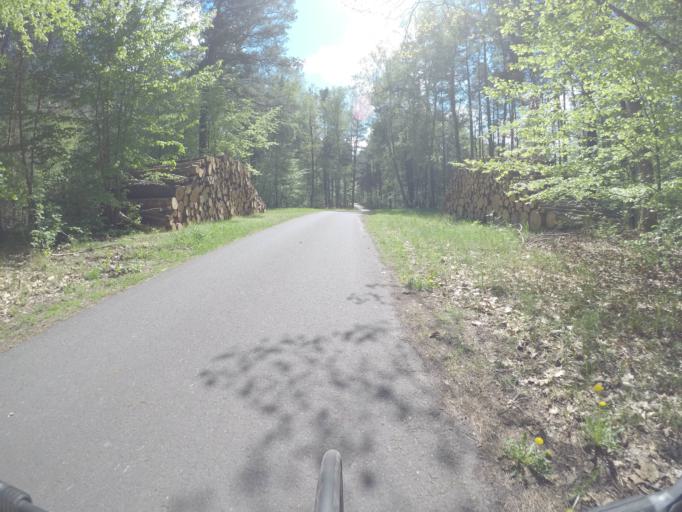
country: DE
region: Brandenburg
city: Rudnitz
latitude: 52.7352
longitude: 13.6090
